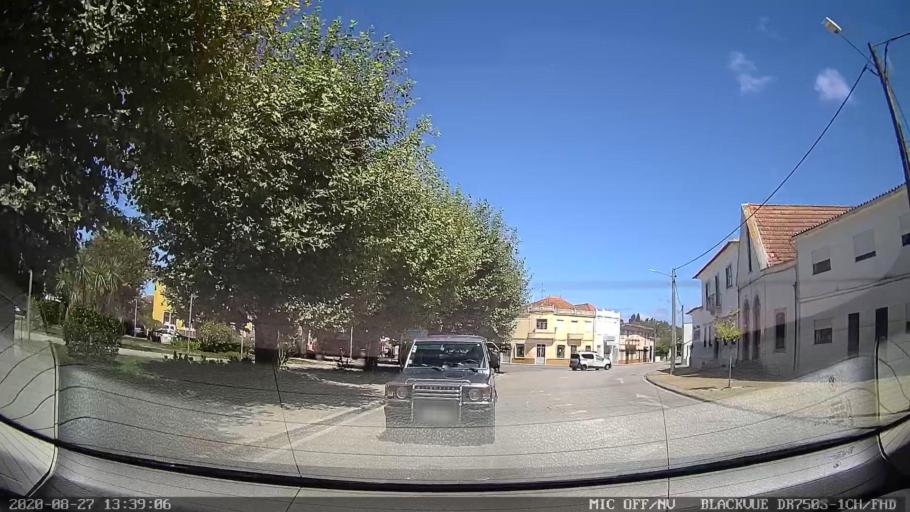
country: PT
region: Coimbra
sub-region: Mira
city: Mira
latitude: 40.4430
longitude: -8.7287
